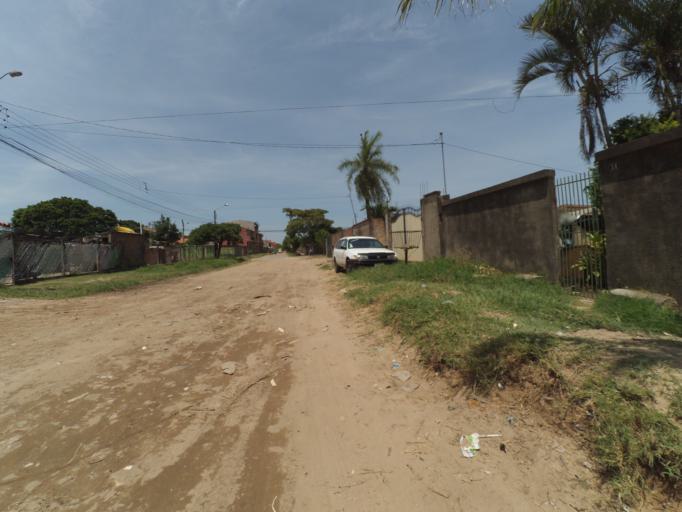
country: BO
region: Santa Cruz
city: Santa Cruz de la Sierra
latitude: -17.8295
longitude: -63.2331
